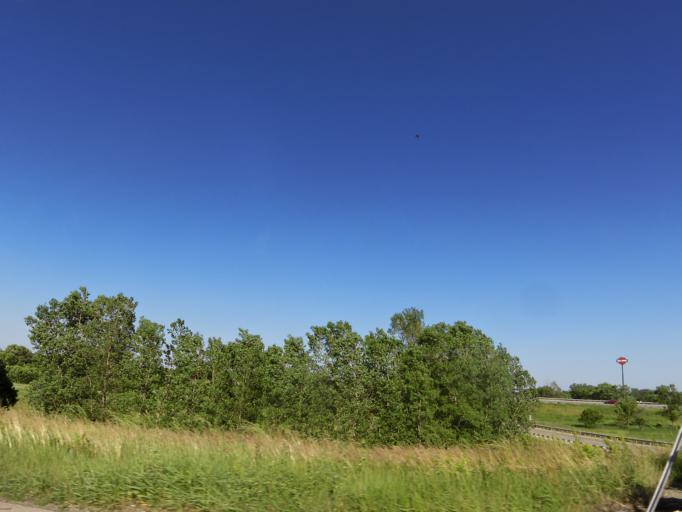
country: US
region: Wisconsin
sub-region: Dane County
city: McFarland
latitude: 43.0472
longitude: -89.2760
